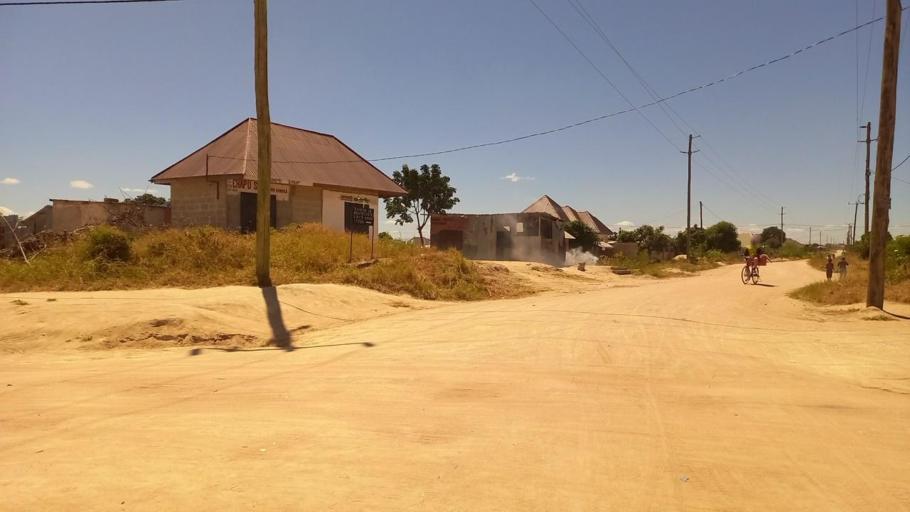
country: TZ
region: Dodoma
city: Dodoma
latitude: -6.1328
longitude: 35.7190
